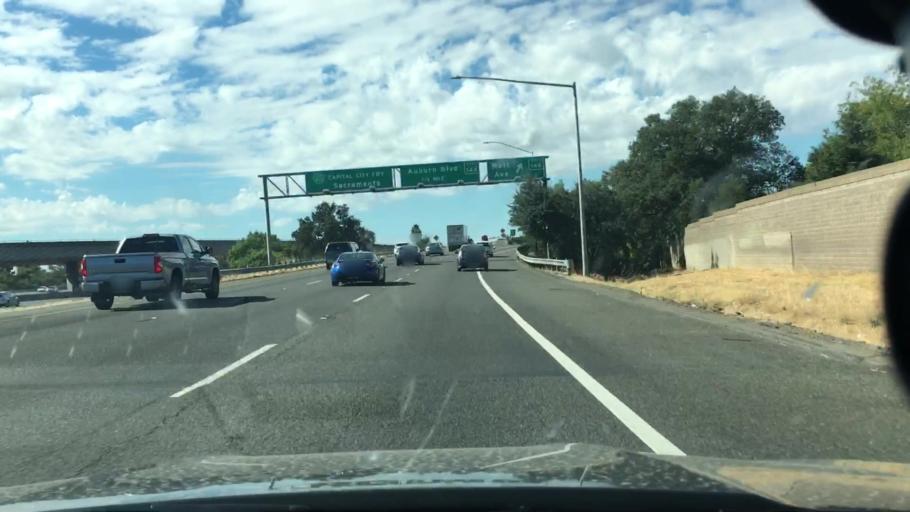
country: US
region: California
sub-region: Sacramento County
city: North Highlands
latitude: 38.6494
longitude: -121.3735
